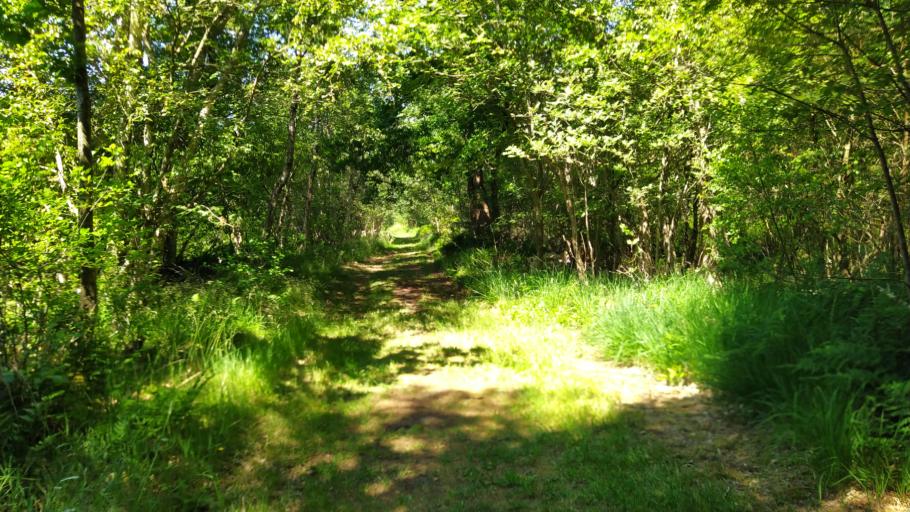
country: DE
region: Lower Saxony
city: Oldendorf
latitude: 53.5615
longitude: 9.2539
